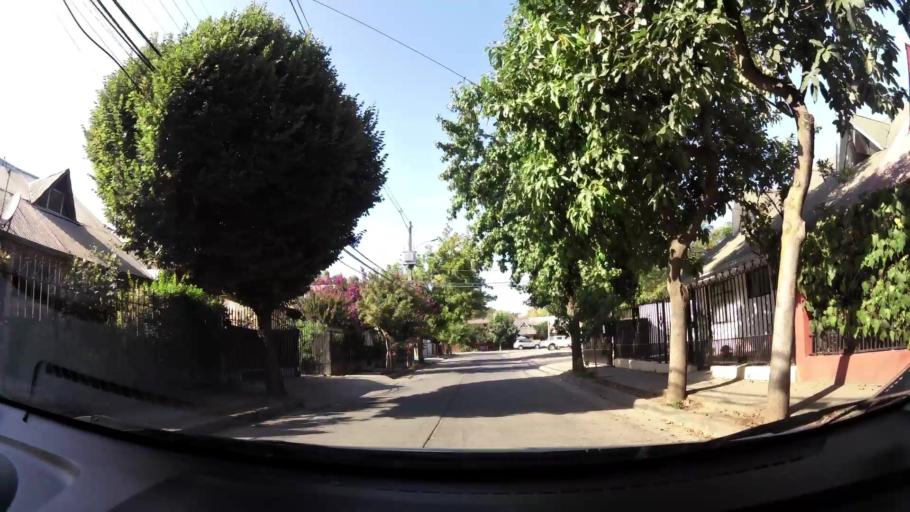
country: CL
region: Maule
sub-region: Provincia de Talca
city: Talca
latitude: -35.4106
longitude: -71.6635
